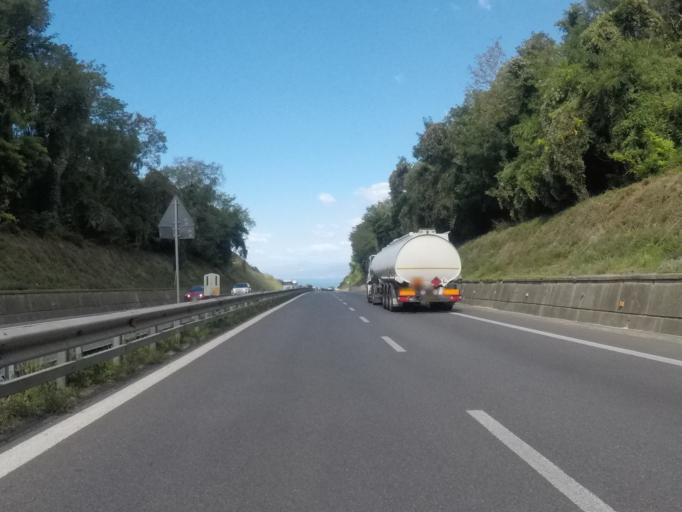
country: IT
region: Calabria
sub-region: Provincia di Vibo-Valentia
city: Sant'Onofrio
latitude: 38.7090
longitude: 16.1539
